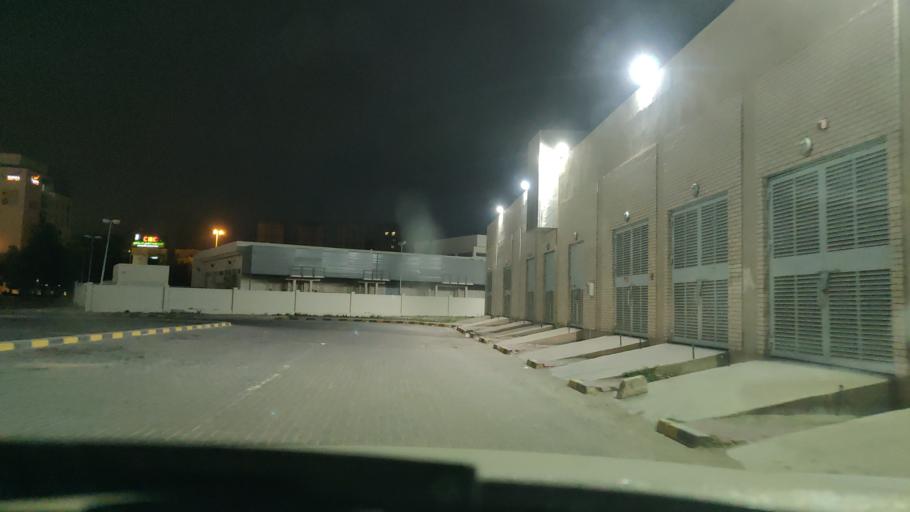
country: KW
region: Muhafazat al Jahra'
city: Al Jahra'
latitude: 29.3390
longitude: 47.6793
